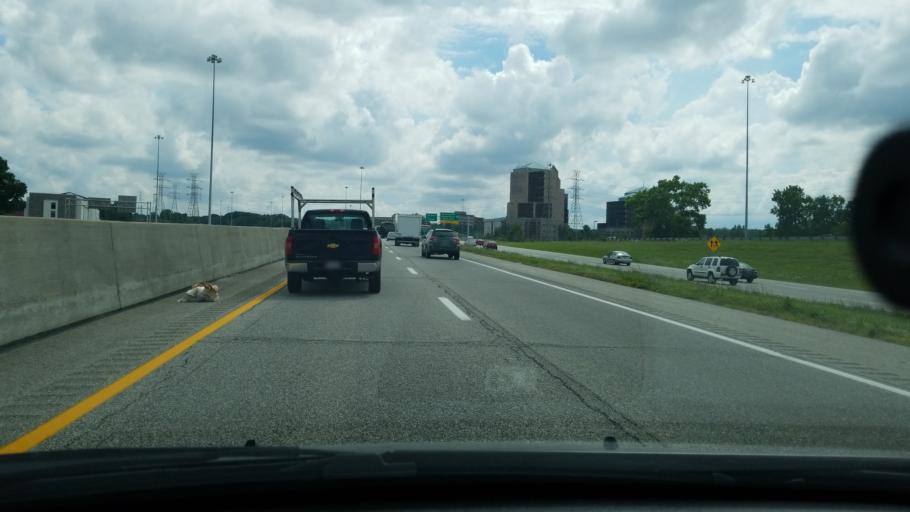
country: US
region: Ohio
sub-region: Cuyahoga County
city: Seven Hills
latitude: 41.4019
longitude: -81.6501
